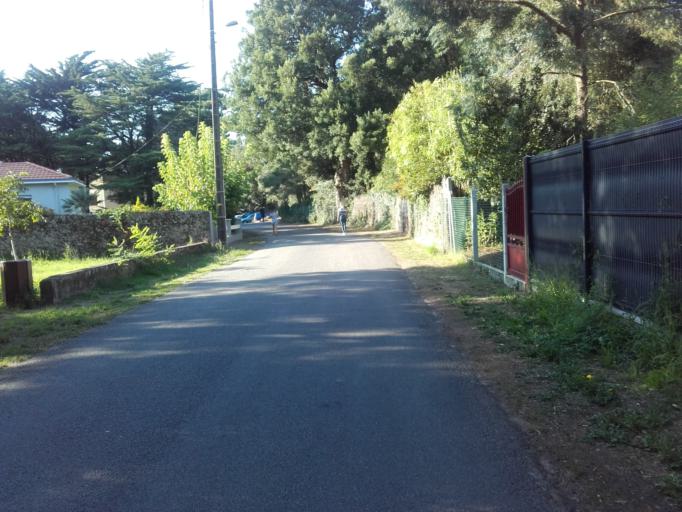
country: FR
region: Pays de la Loire
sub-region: Departement de la Loire-Atlantique
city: Saint-Brevin-les-Pins
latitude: 47.2342
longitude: -2.1781
